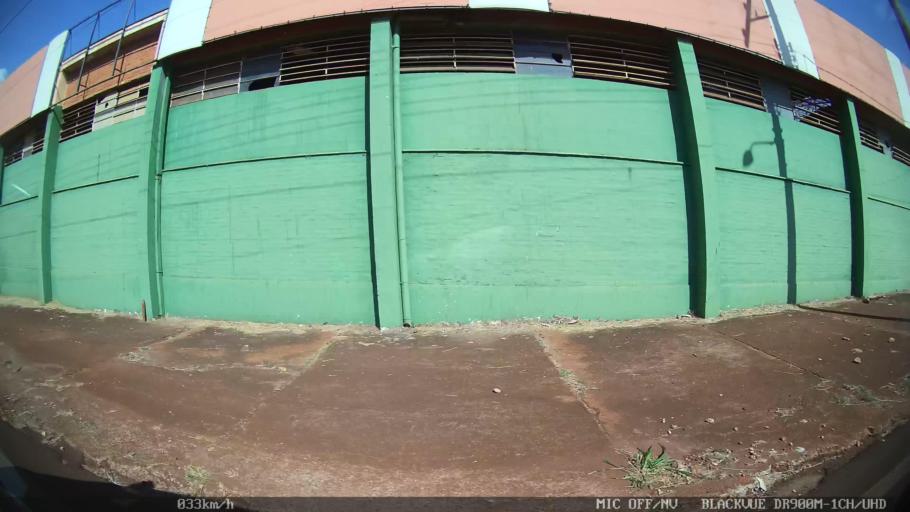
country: BR
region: Sao Paulo
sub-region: Ribeirao Preto
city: Ribeirao Preto
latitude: -21.1785
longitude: -47.8320
